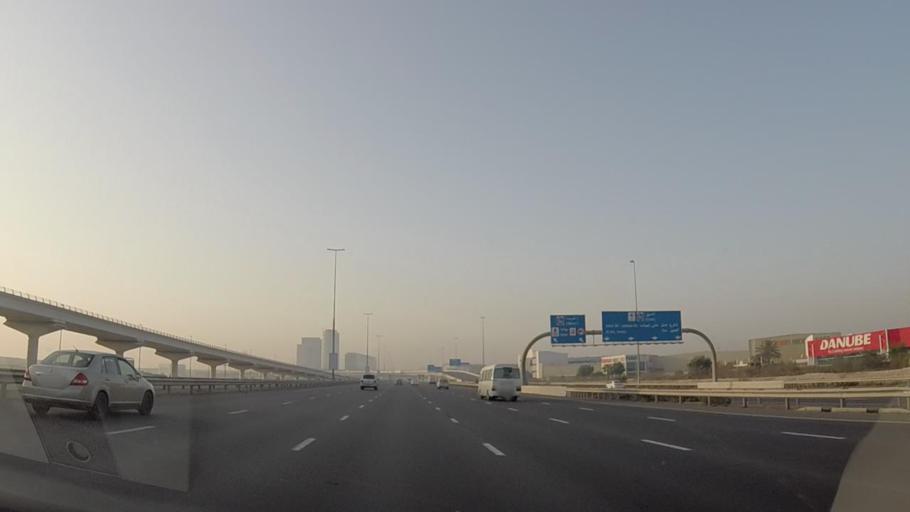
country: AE
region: Dubai
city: Dubai
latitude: 24.9965
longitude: 55.0943
